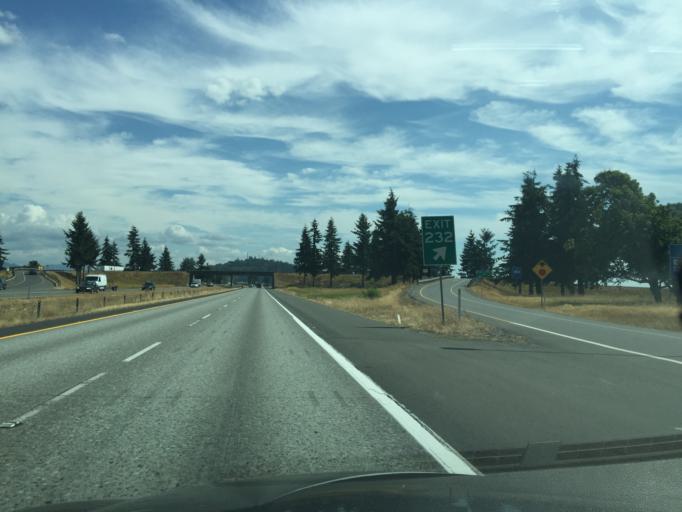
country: US
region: Washington
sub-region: Skagit County
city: Burlington
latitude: 48.5100
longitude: -122.3409
